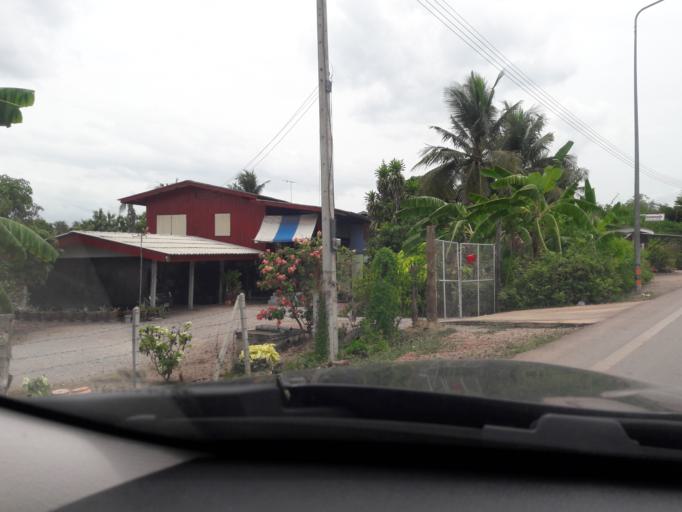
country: TH
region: Ratchaburi
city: Damnoen Saduak
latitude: 13.5930
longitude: 99.9369
